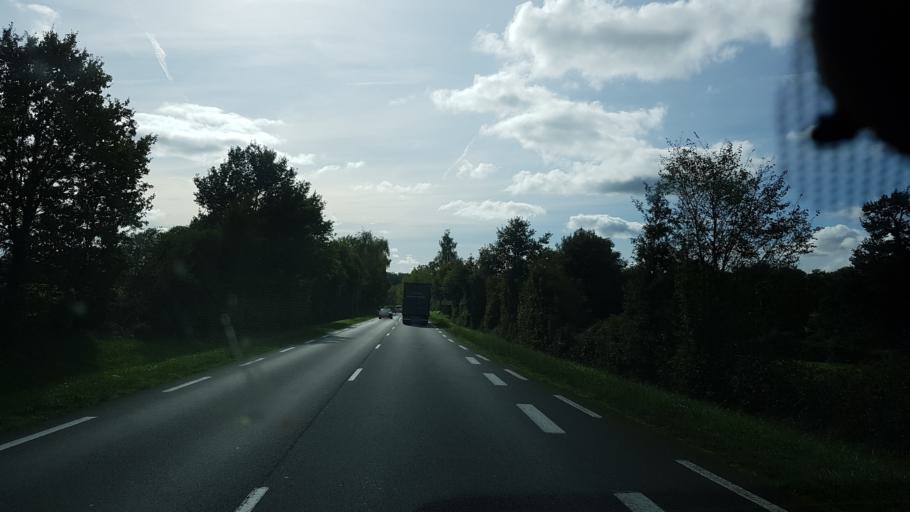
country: FR
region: Poitou-Charentes
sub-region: Departement de la Charente
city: Confolens
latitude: 46.0209
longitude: 0.6506
